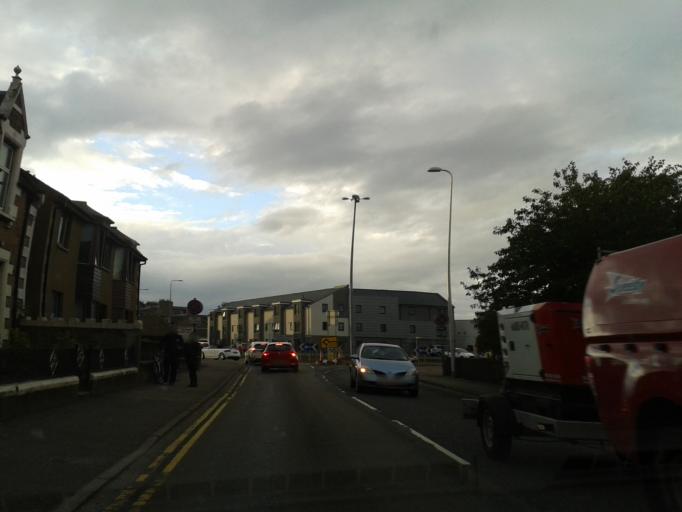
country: GB
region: Scotland
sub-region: Highland
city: Inverness
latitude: 57.4797
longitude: -4.2367
